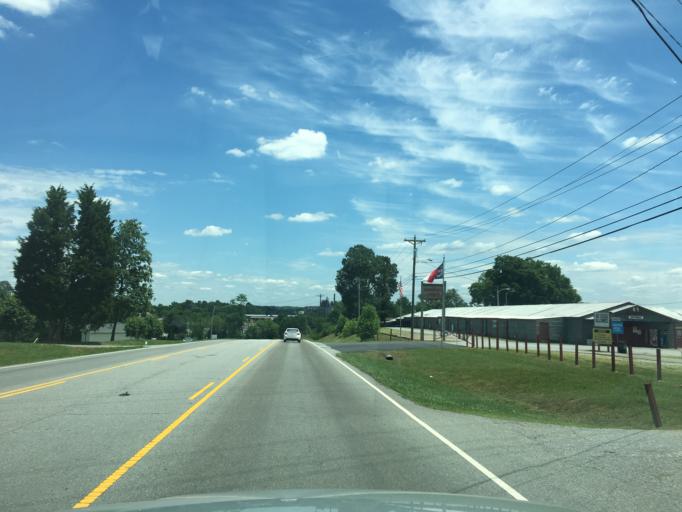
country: US
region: North Carolina
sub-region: Burke County
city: Glen Alpine
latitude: 35.7262
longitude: -81.7403
